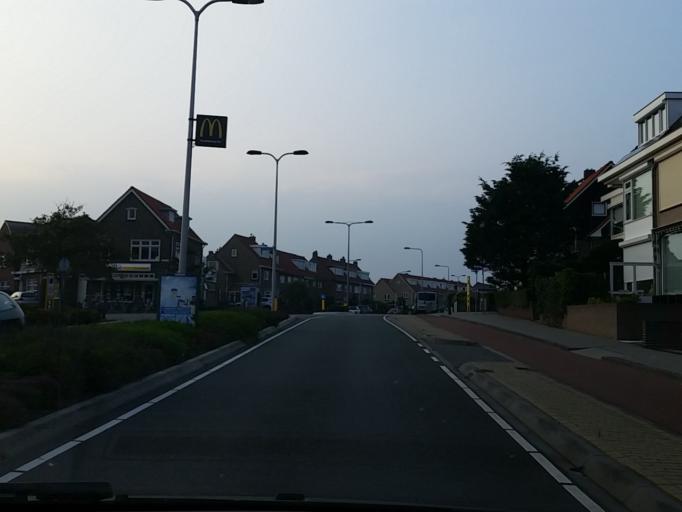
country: NL
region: South Holland
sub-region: Gemeente Noordwijk
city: Noordwijk-Binnen
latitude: 52.2444
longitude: 4.4409
